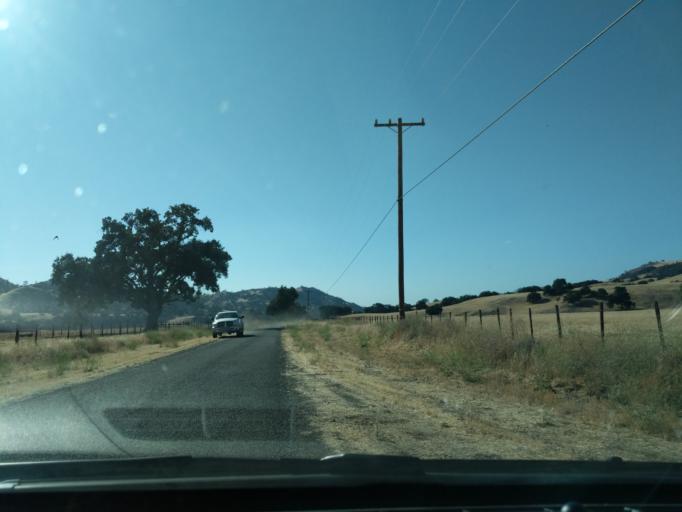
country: US
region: California
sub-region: San Luis Obispo County
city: San Miguel
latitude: 36.1142
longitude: -120.7240
